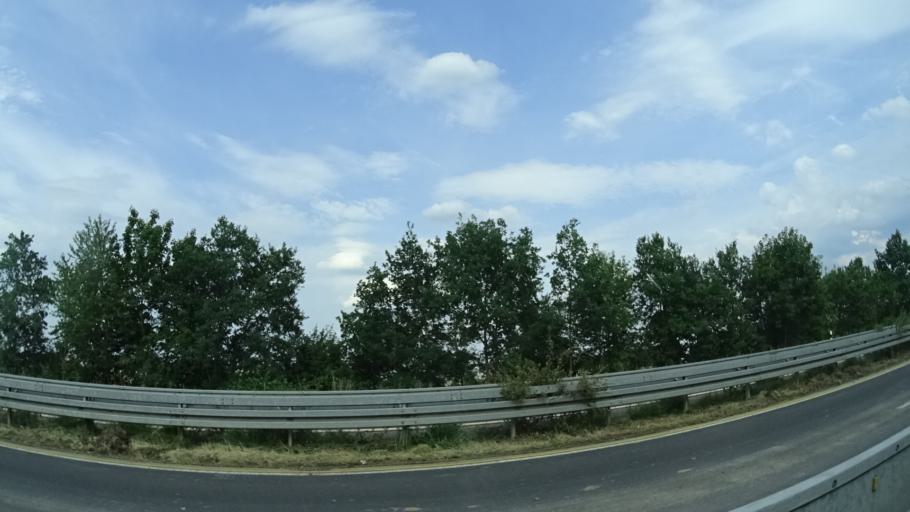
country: DE
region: Hesse
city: Dieburg
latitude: 49.9159
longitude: 8.8471
